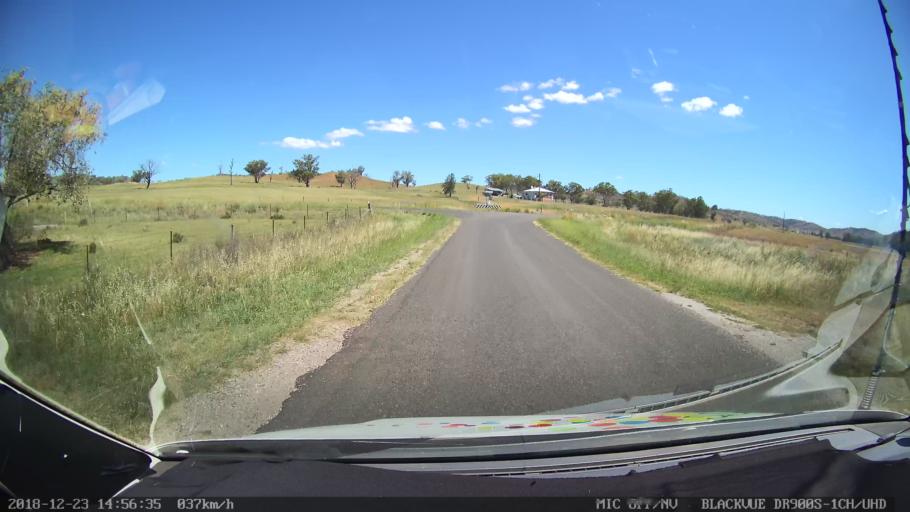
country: AU
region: New South Wales
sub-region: Tamworth Municipality
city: Manilla
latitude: -30.7048
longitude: 150.8296
